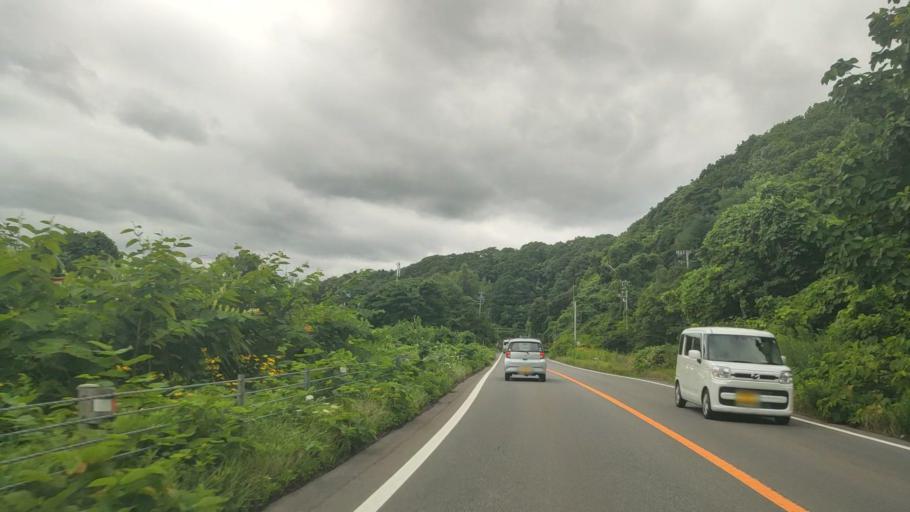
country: JP
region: Hokkaido
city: Date
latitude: 42.5681
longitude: 140.7359
